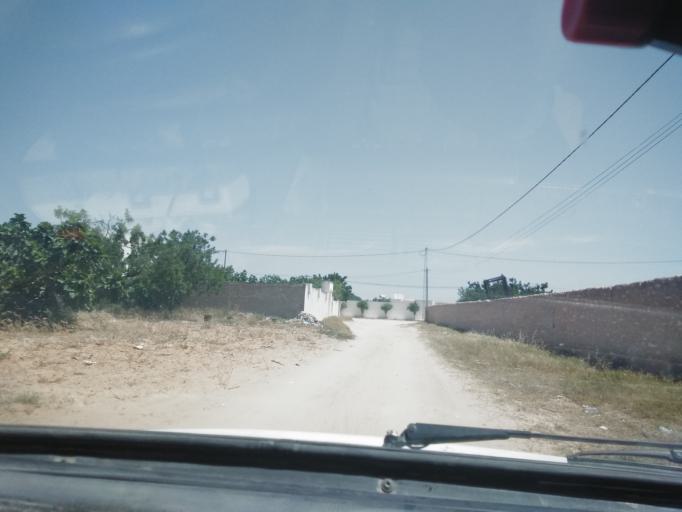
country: TN
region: Safaqis
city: Al Qarmadah
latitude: 34.8058
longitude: 10.7765
